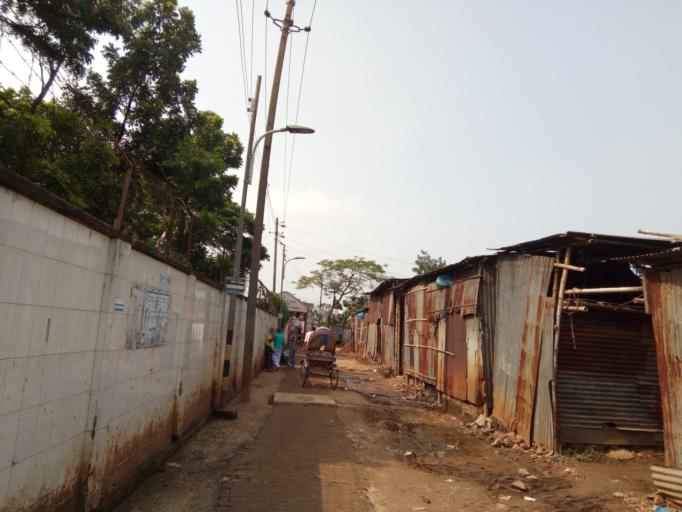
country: BD
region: Dhaka
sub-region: Dhaka
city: Dhaka
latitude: 23.6971
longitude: 90.4293
